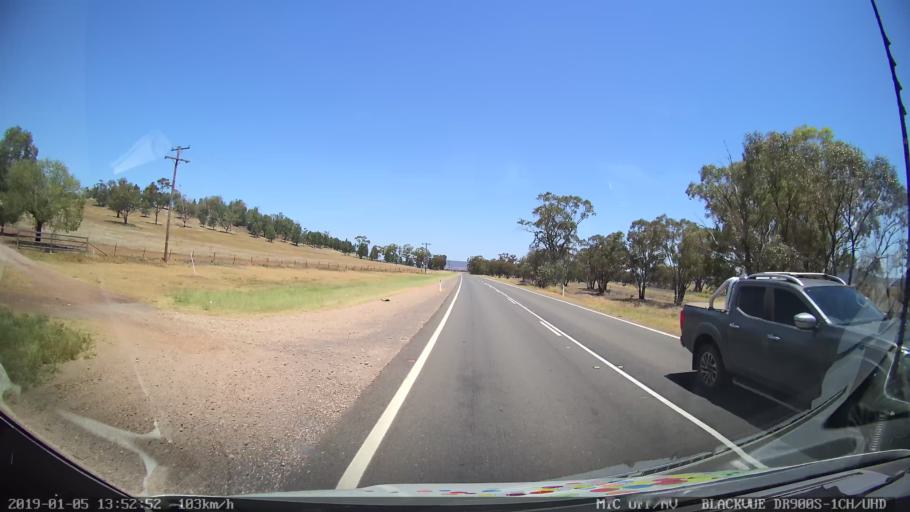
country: AU
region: New South Wales
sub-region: Gunnedah
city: Gunnedah
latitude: -31.0665
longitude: 150.2768
